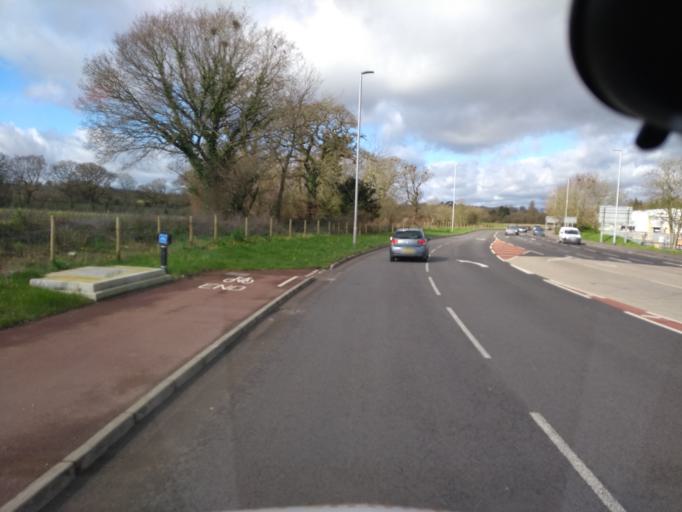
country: GB
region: England
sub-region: Somerset
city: Yeovil
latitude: 50.9332
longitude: -2.6645
